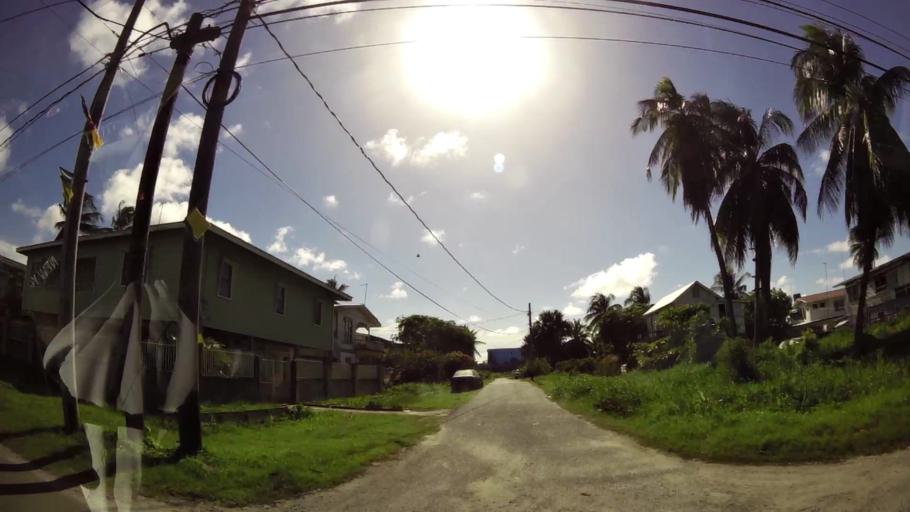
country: GY
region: Demerara-Mahaica
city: Georgetown
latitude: 6.8211
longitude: -58.1325
